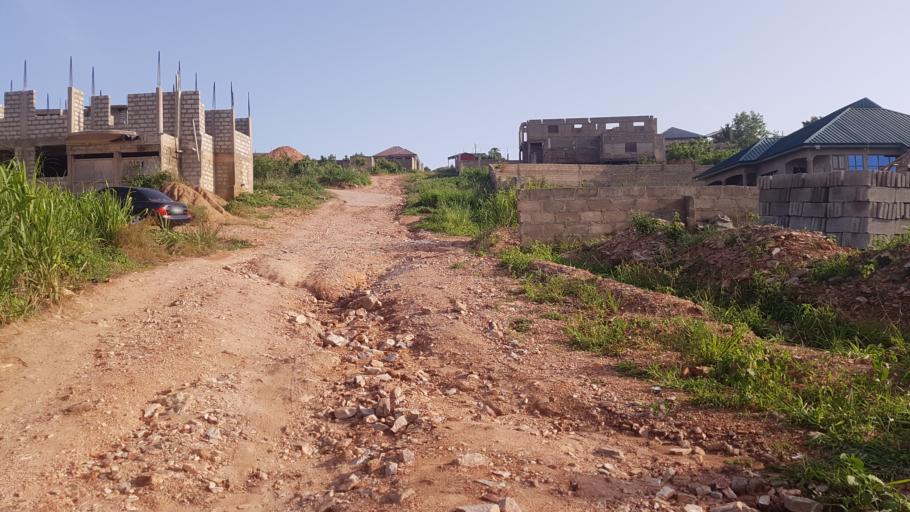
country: GH
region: Greater Accra
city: Gbawe
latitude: 5.5209
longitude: -0.3390
